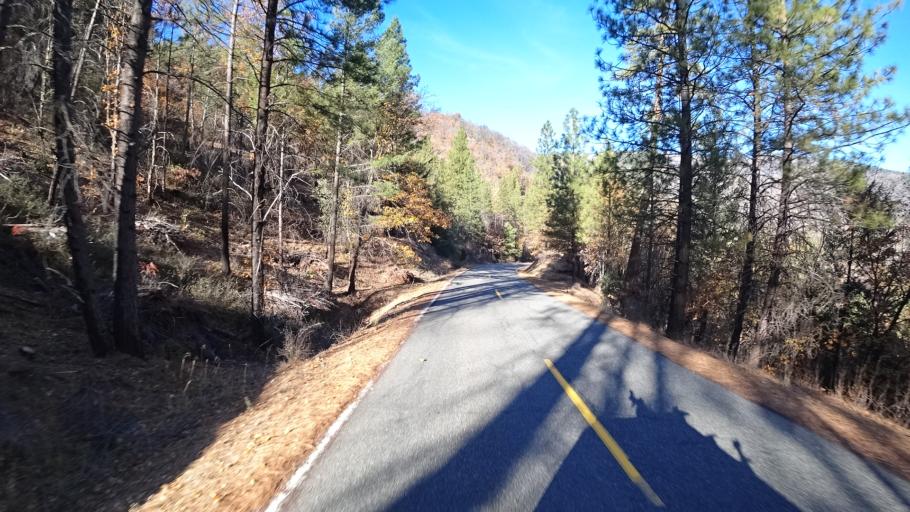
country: US
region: California
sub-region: Siskiyou County
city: Yreka
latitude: 41.9064
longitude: -122.8336
